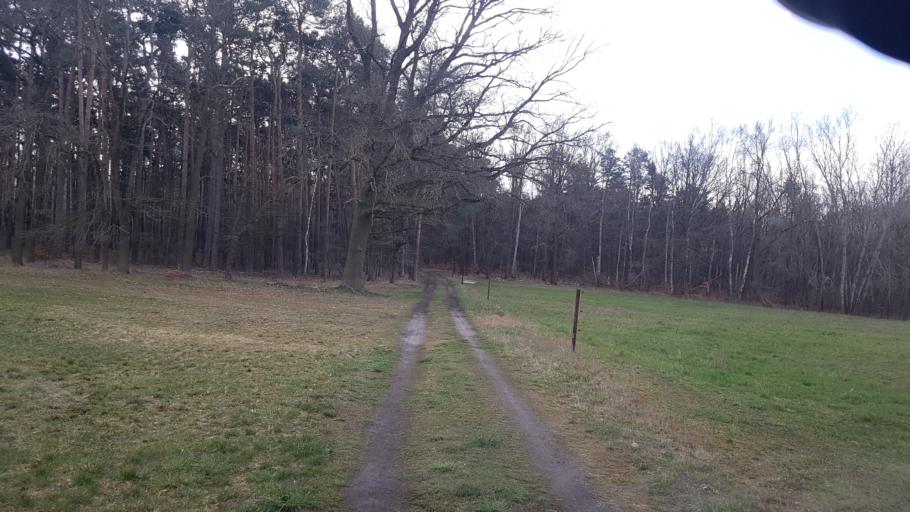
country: DE
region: Brandenburg
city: Doberlug-Kirchhain
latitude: 51.6425
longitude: 13.5273
